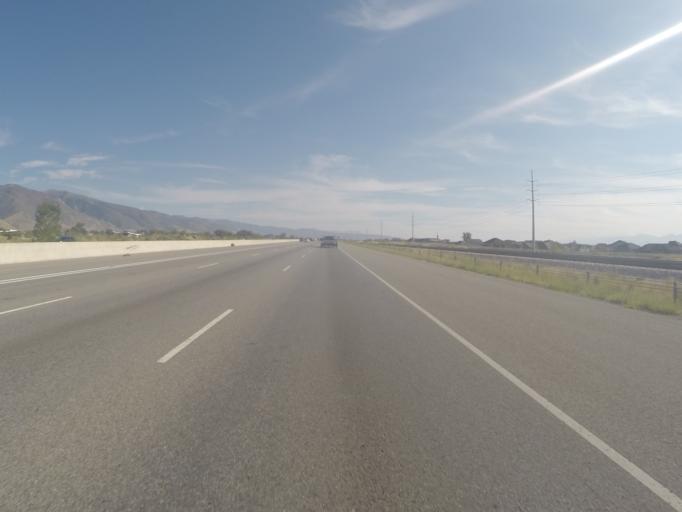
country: US
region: Utah
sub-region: Davis County
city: Kaysville
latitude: 41.0252
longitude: -111.9453
